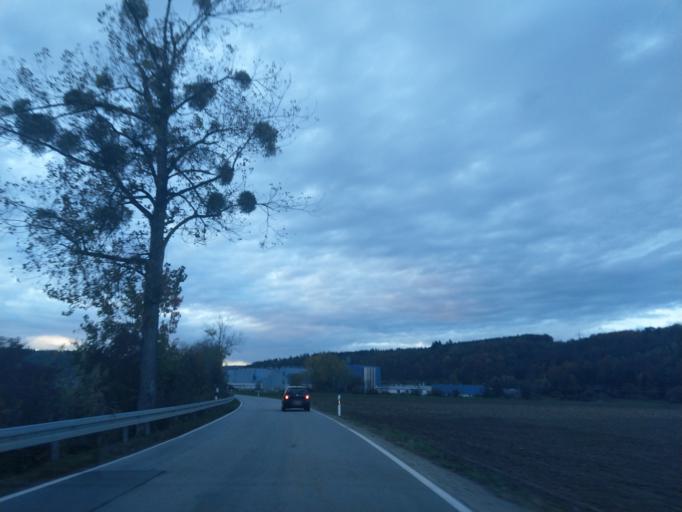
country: DE
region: Bavaria
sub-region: Lower Bavaria
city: Niederalteich
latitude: 48.7873
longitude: 13.0188
